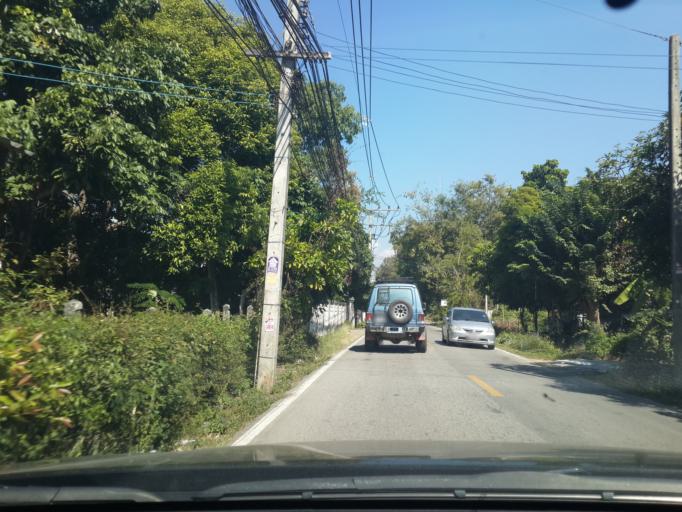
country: TH
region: Chiang Mai
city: San Sai
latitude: 18.8633
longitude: 99.0925
